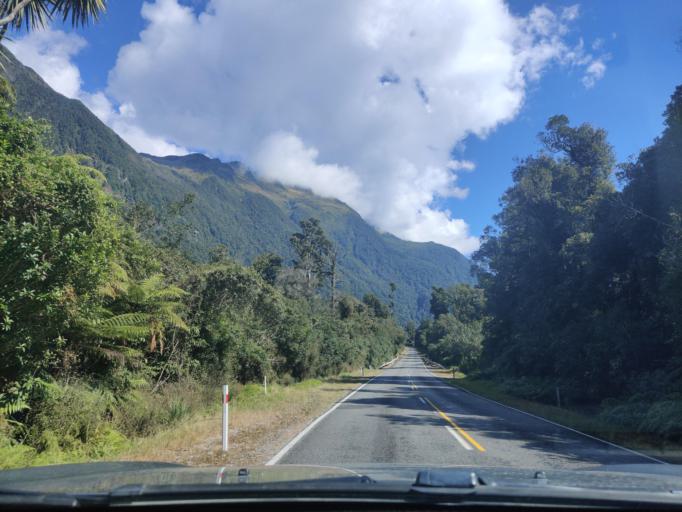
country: NZ
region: Otago
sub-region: Queenstown-Lakes District
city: Wanaka
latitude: -43.9695
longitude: 169.1799
